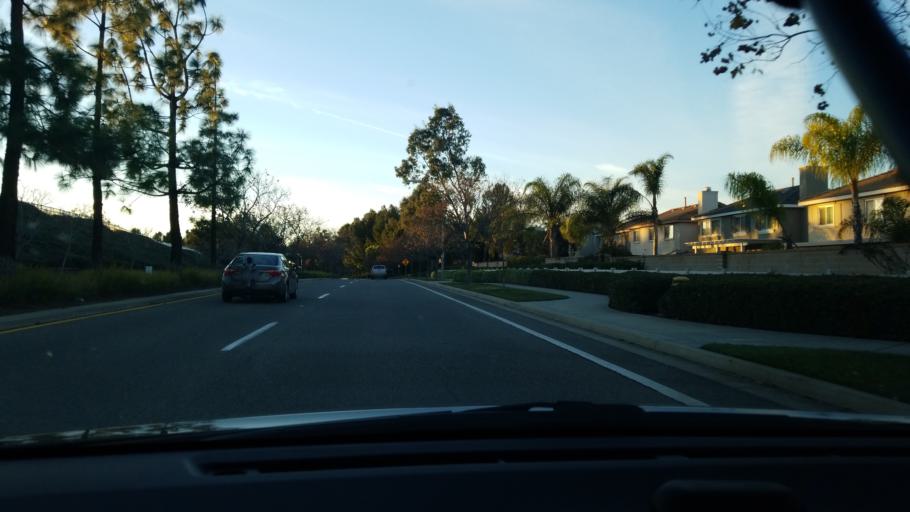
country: US
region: California
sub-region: Riverside County
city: Temecula
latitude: 33.4888
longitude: -117.0853
